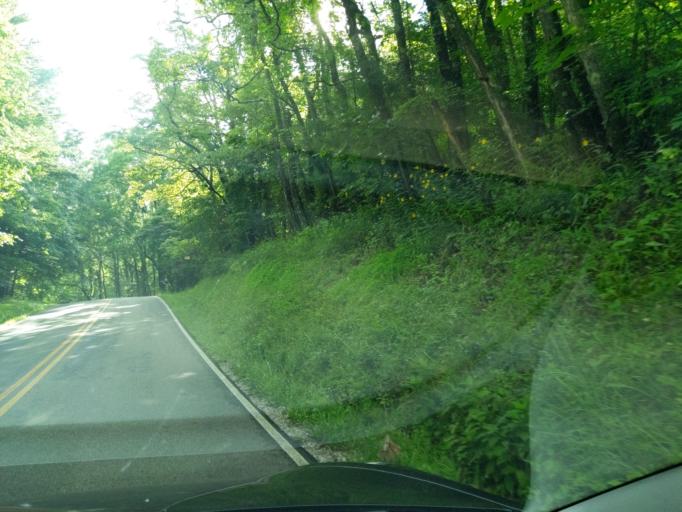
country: US
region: Ohio
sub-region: Fairfield County
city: Lancaster
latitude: 39.5568
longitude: -82.6210
